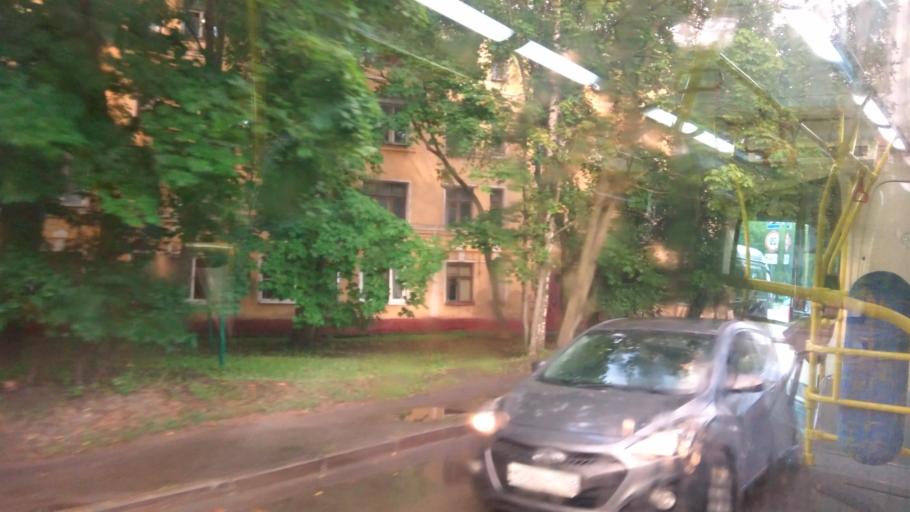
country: RU
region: Moskovskaya
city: Marfino
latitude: 55.7199
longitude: 37.3943
